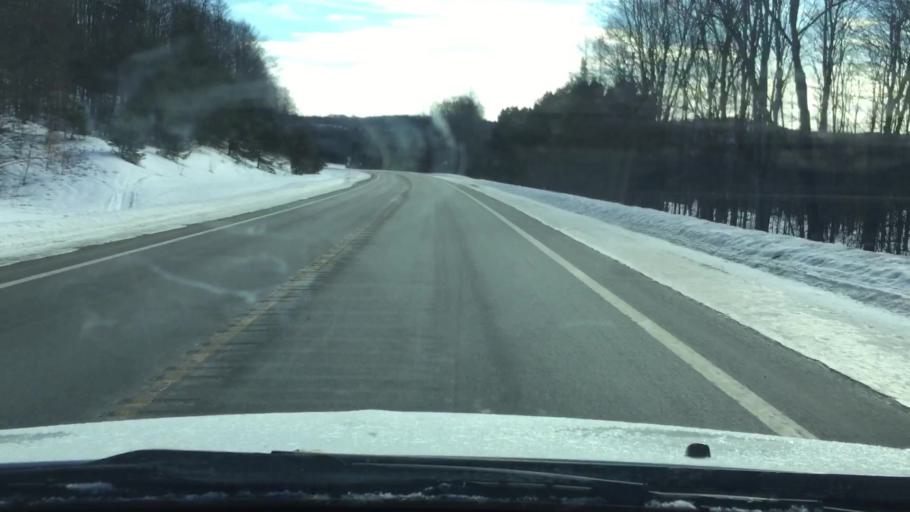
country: US
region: Michigan
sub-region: Antrim County
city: Mancelona
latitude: 44.9722
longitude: -85.0550
